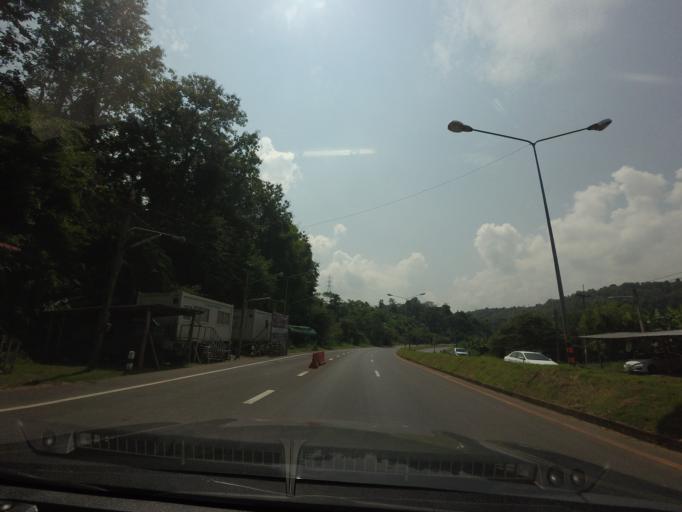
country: TH
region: Phrae
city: Den Chai
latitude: 17.8815
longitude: 100.0464
